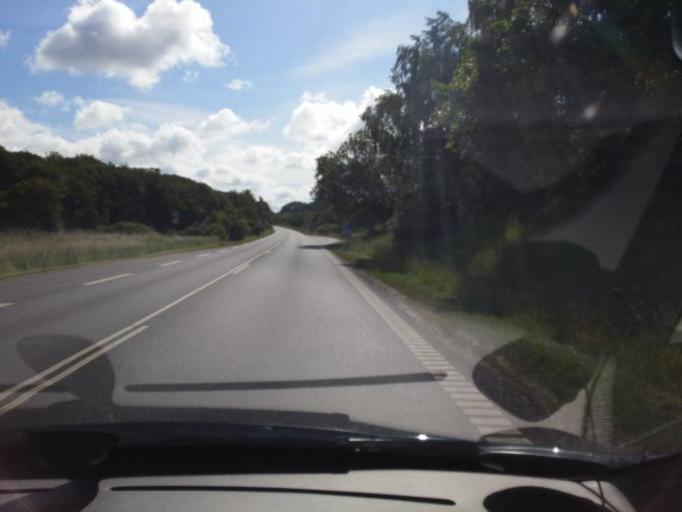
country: DK
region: Capital Region
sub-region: Hillerod Kommune
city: Hillerod
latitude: 55.9549
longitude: 12.2665
